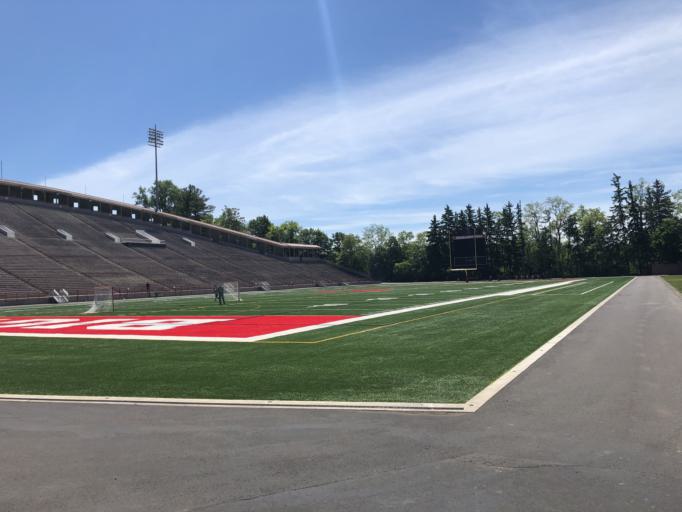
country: US
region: New York
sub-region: Tompkins County
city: East Ithaca
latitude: 42.4447
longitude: -76.4790
